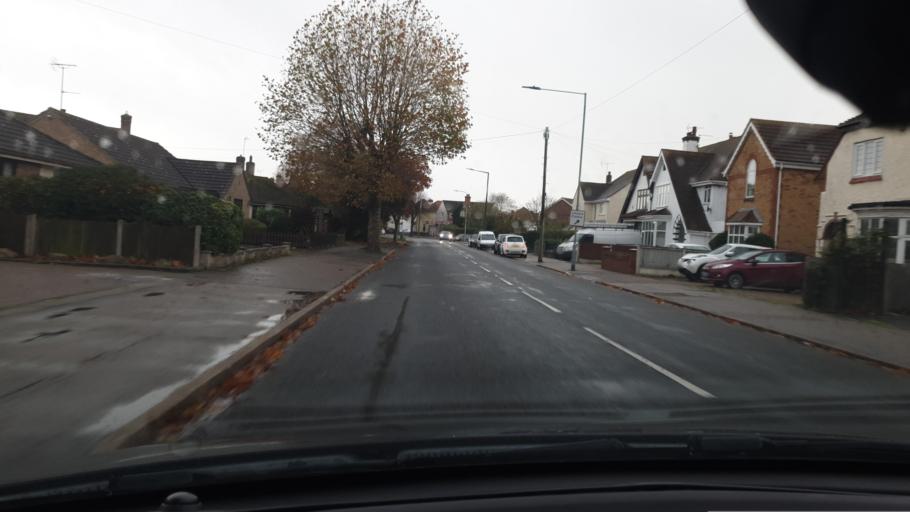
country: GB
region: England
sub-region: Essex
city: Clacton-on-Sea
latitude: 51.7949
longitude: 1.1631
